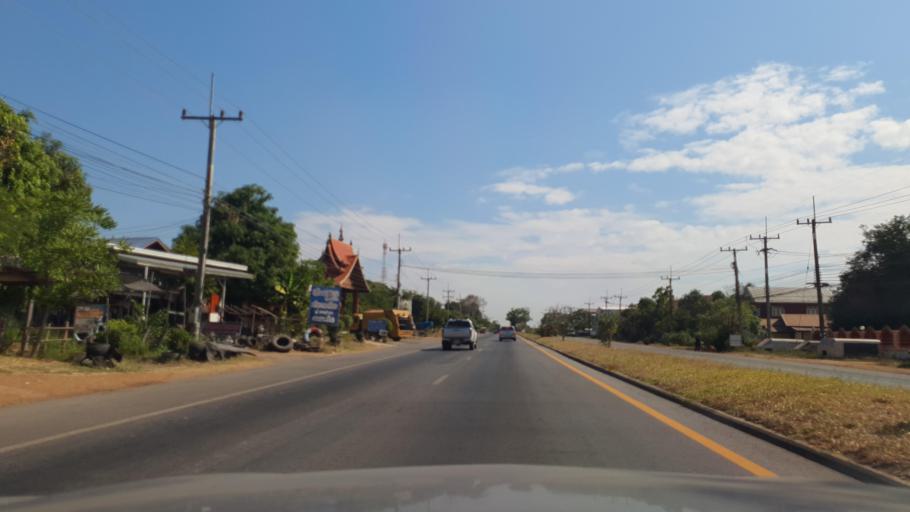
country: TH
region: Maha Sarakham
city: Chiang Yuen
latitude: 16.3784
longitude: 103.1852
